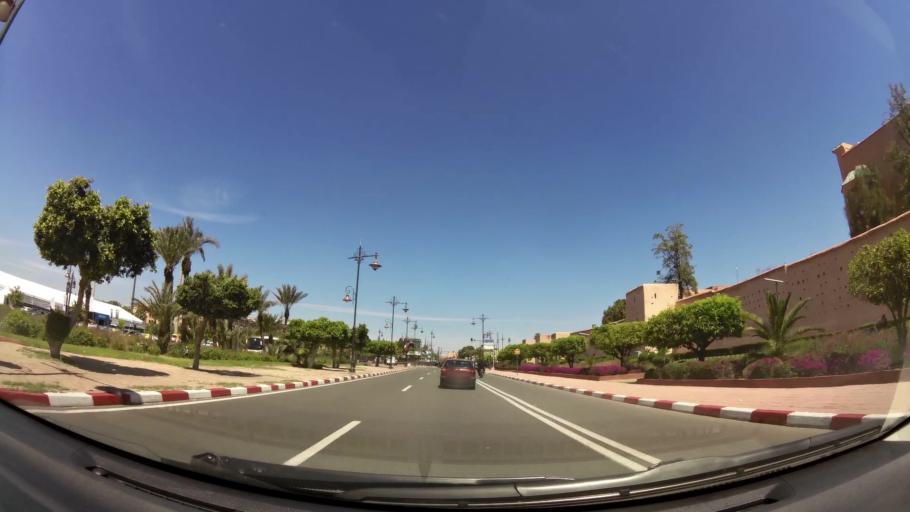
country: MA
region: Marrakech-Tensift-Al Haouz
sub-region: Marrakech
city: Marrakesh
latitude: 31.6206
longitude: -7.9986
